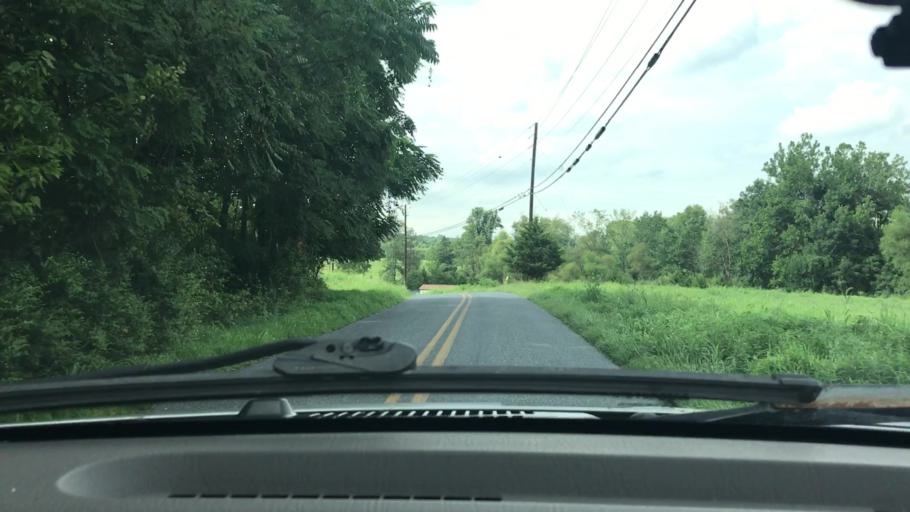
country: US
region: Pennsylvania
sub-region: Lancaster County
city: Elizabethtown
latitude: 40.1714
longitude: -76.6198
